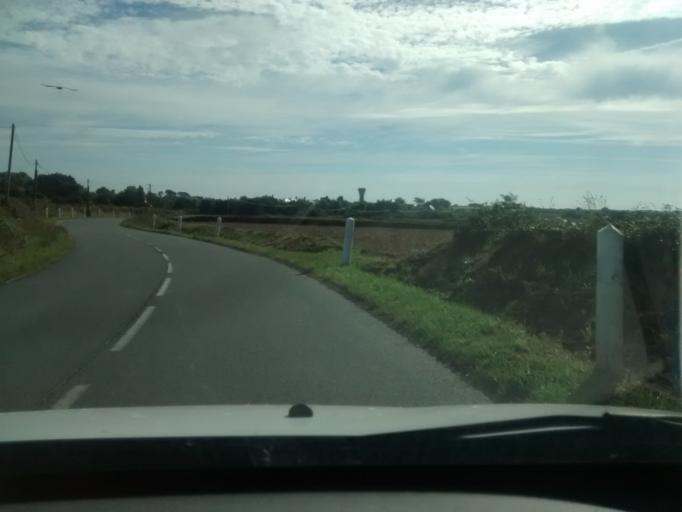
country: FR
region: Brittany
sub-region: Departement des Cotes-d'Armor
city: Plougrescant
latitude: 48.8305
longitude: -3.2428
